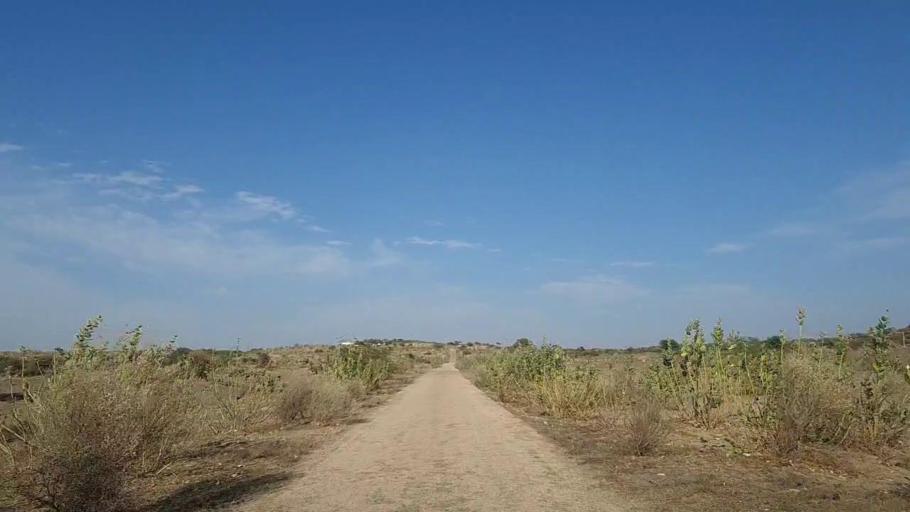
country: PK
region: Sindh
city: Naukot
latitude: 24.8386
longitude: 69.4779
